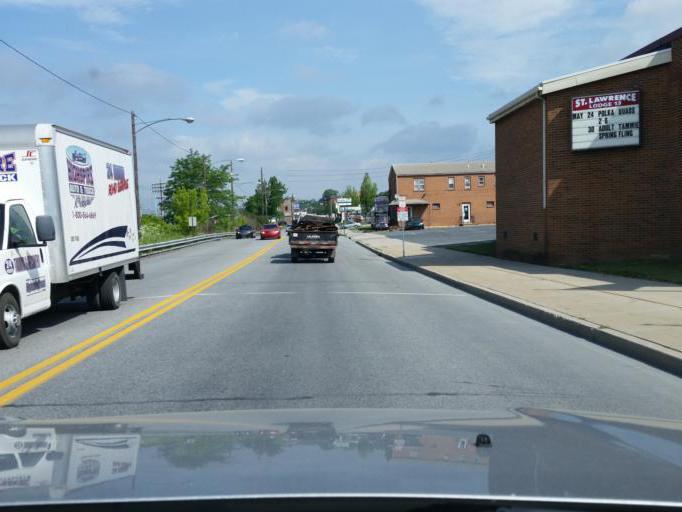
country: US
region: Pennsylvania
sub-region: Dauphin County
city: Enhaut
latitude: 40.2285
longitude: -76.8317
